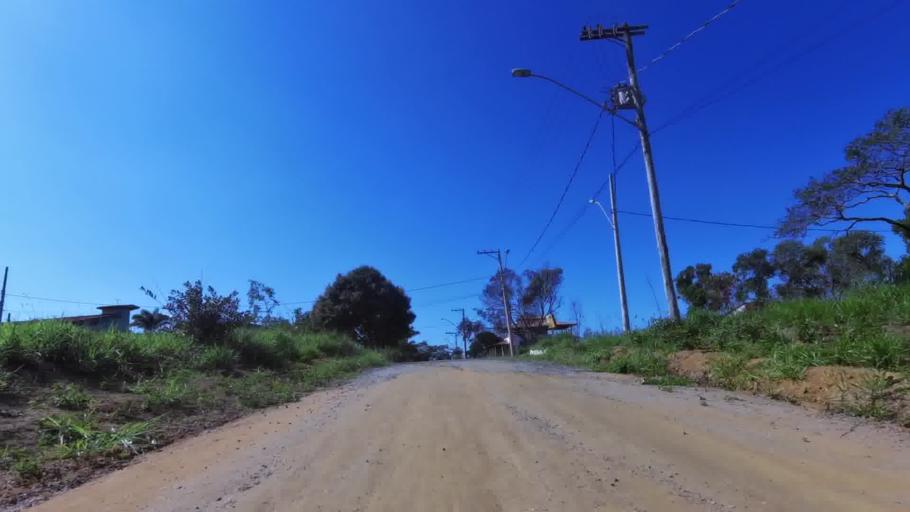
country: BR
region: Espirito Santo
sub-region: Guarapari
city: Guarapari
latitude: -20.7341
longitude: -40.5485
